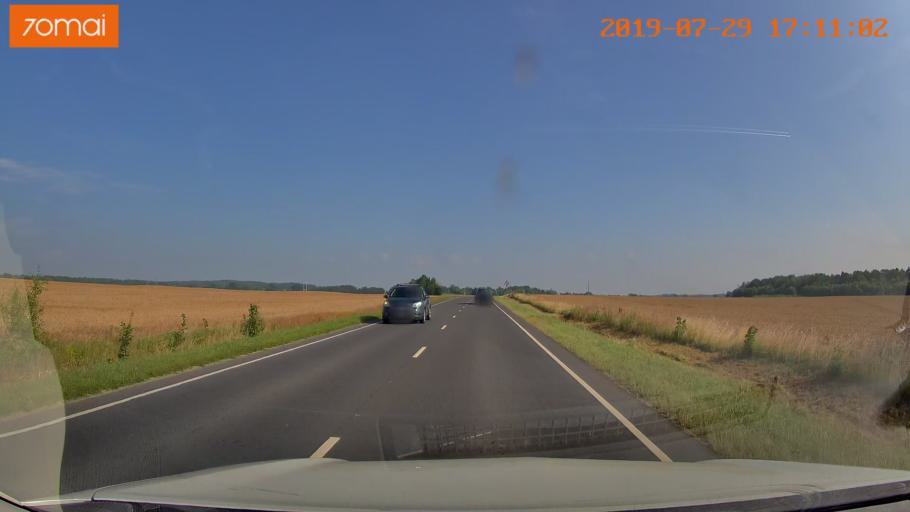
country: RU
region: Kaliningrad
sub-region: Gorod Kaliningrad
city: Kaliningrad
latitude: 54.7982
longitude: 20.3753
